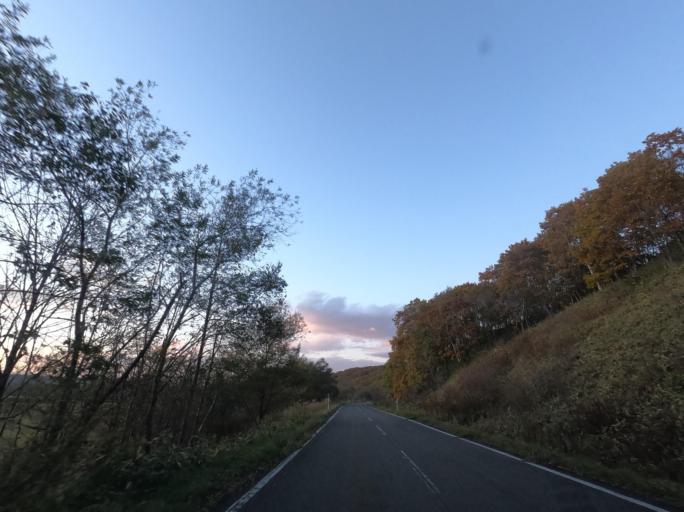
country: JP
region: Hokkaido
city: Kushiro
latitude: 43.2113
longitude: 144.4544
